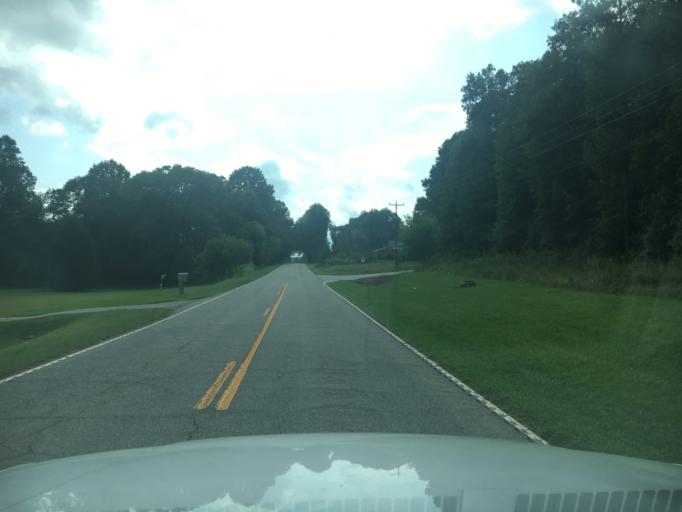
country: US
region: South Carolina
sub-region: Anderson County
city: Belton
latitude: 34.5355
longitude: -82.4585
